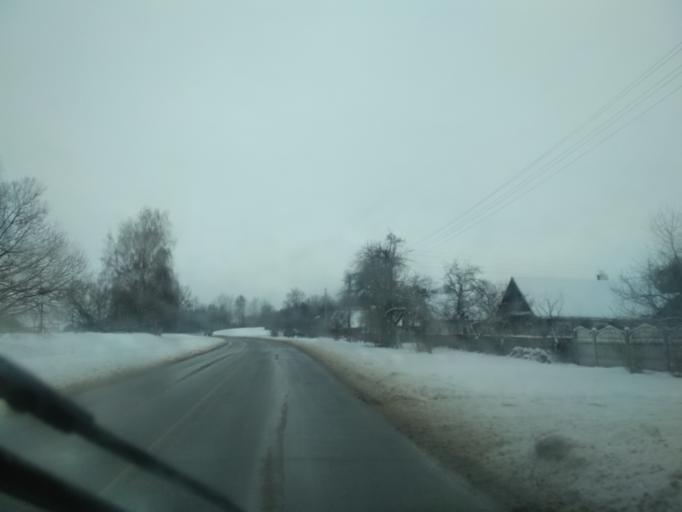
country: BY
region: Minsk
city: Mar''ina Horka
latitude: 53.5272
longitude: 28.1327
